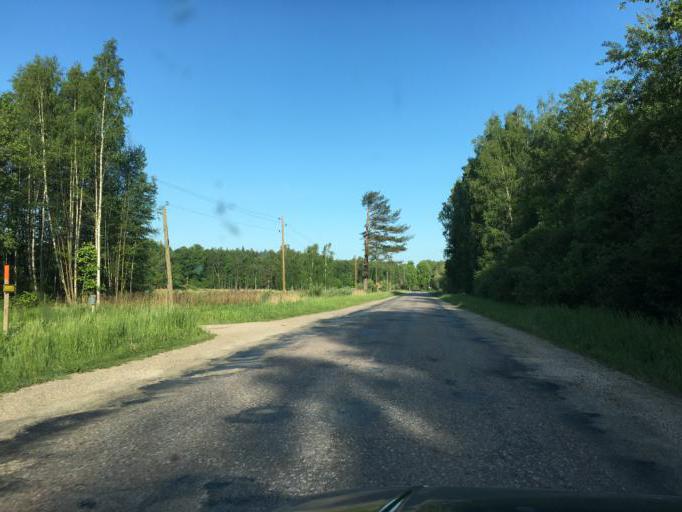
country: LV
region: Jelgava
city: Jelgava
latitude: 56.6555
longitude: 23.6038
